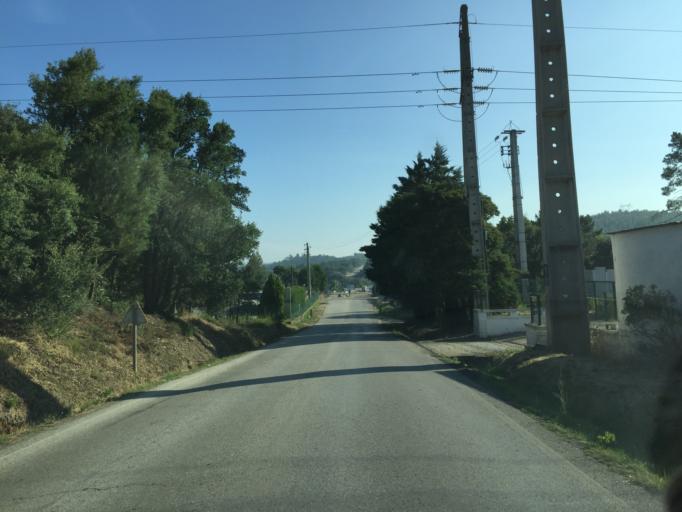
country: PT
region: Santarem
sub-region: Abrantes
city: Alferrarede
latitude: 39.4877
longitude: -8.1793
